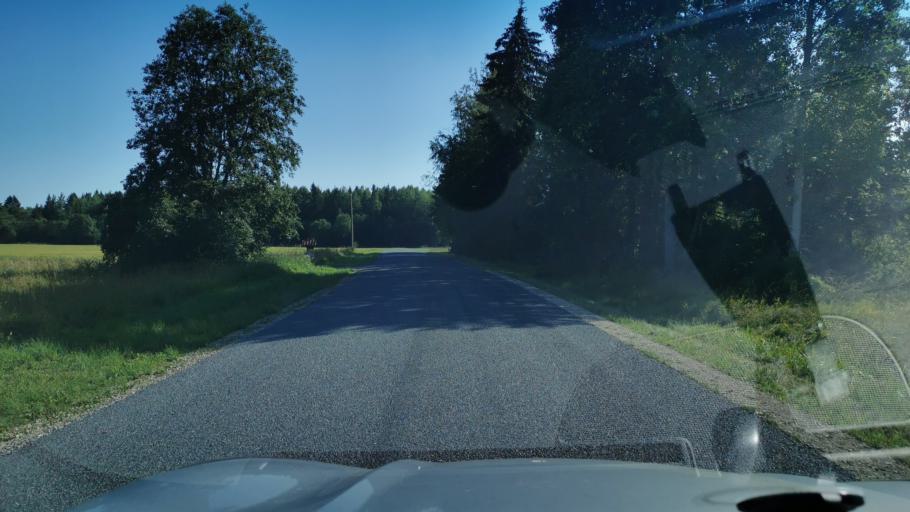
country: EE
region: Harju
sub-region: Paldiski linn
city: Paldiski
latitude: 59.2109
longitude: 24.0212
